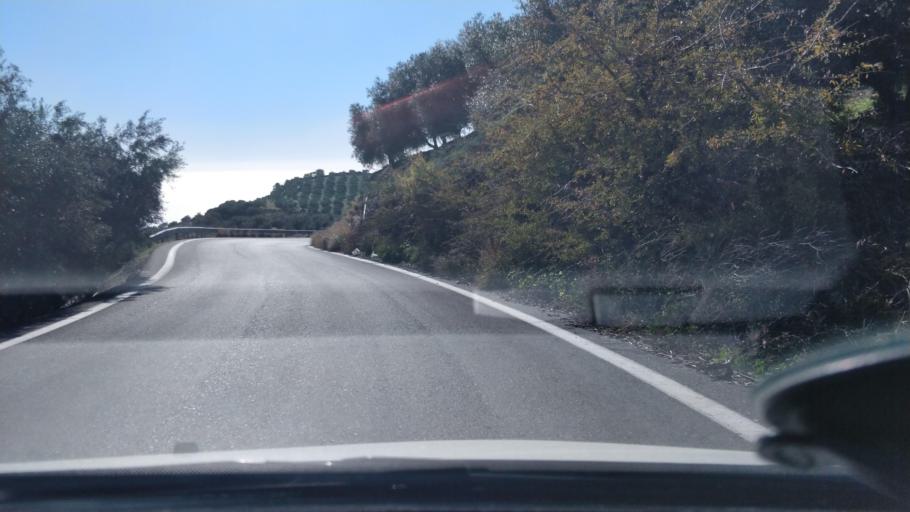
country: GR
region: Crete
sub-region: Nomos Irakleiou
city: Arkalochori
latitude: 35.0083
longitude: 25.4418
